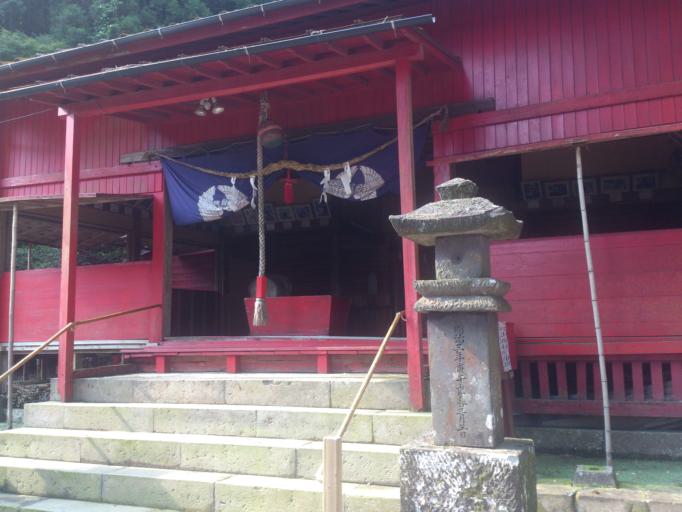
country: JP
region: Kagoshima
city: Kanoya
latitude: 31.3434
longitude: 130.9468
